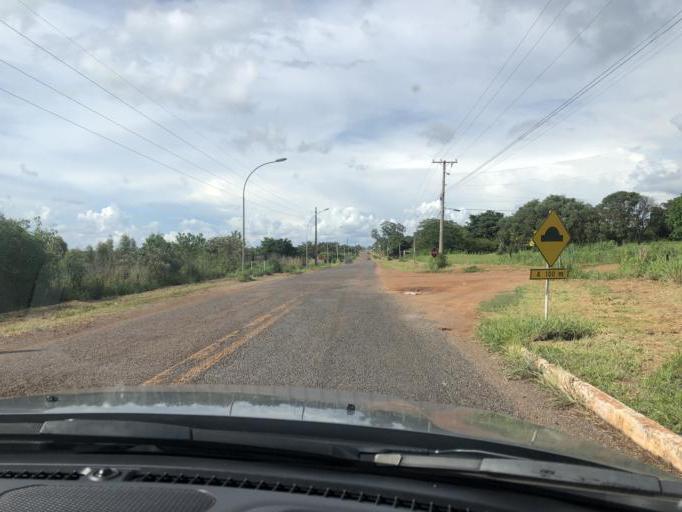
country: BR
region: Federal District
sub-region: Brasilia
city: Brasilia
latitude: -15.7451
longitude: -48.1259
